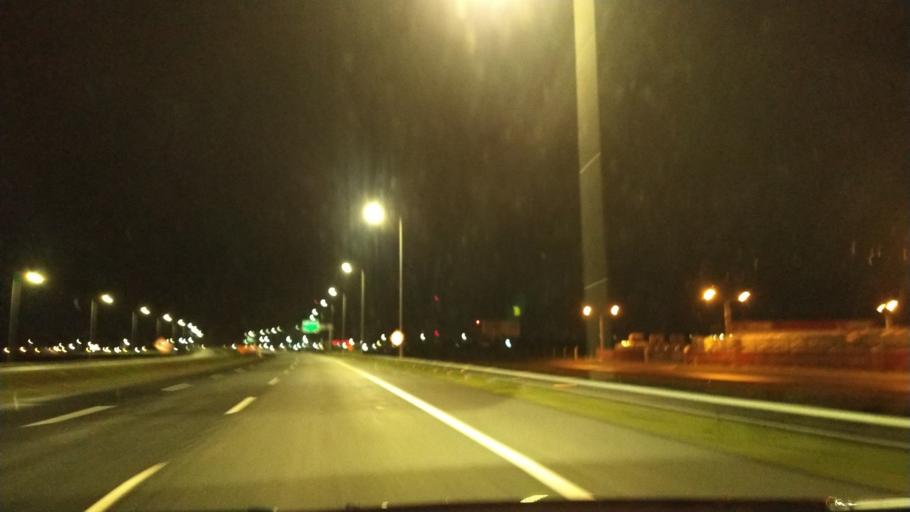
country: AR
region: Cordoba
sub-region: Departamento de Capital
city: Cordoba
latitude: -31.3552
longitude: -64.2108
